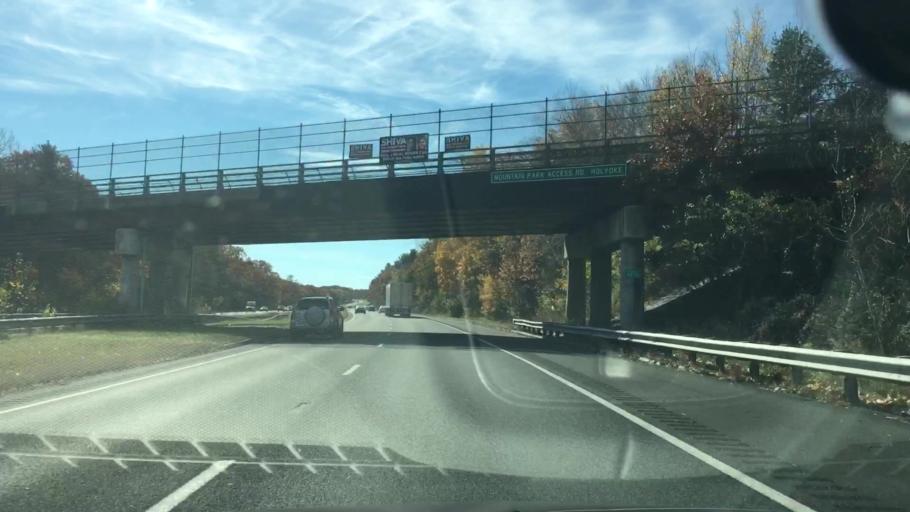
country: US
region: Massachusetts
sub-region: Hampden County
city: Holyoke
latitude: 42.2418
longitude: -72.6294
